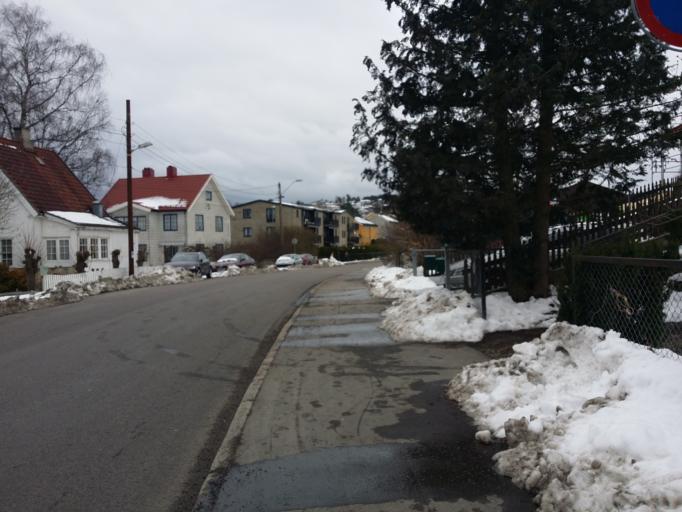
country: NO
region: Oslo
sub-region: Oslo
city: Oslo
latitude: 59.8978
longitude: 10.7803
